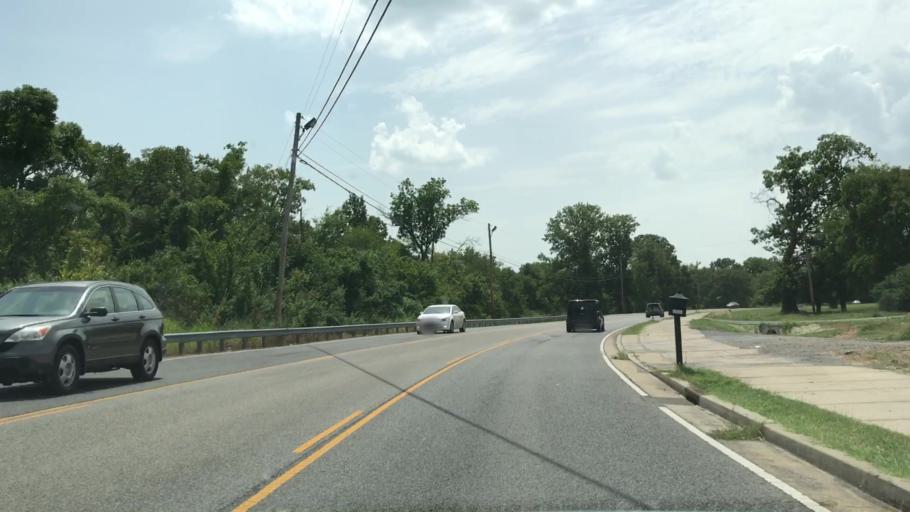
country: US
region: Tennessee
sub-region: Rutherford County
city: Smyrna
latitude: 35.9748
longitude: -86.5577
